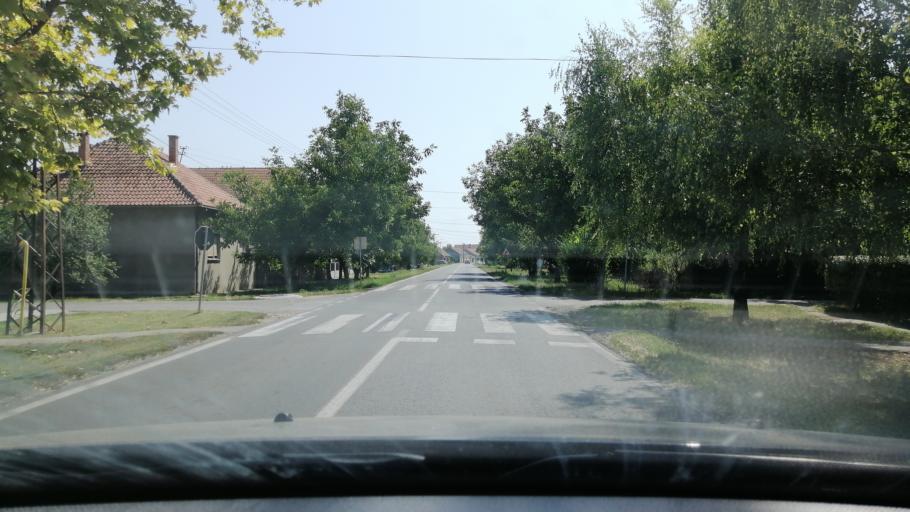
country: RS
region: Autonomna Pokrajina Vojvodina
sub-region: Juznobanatski Okrug
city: Pancevo
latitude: 44.8038
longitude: 20.7123
